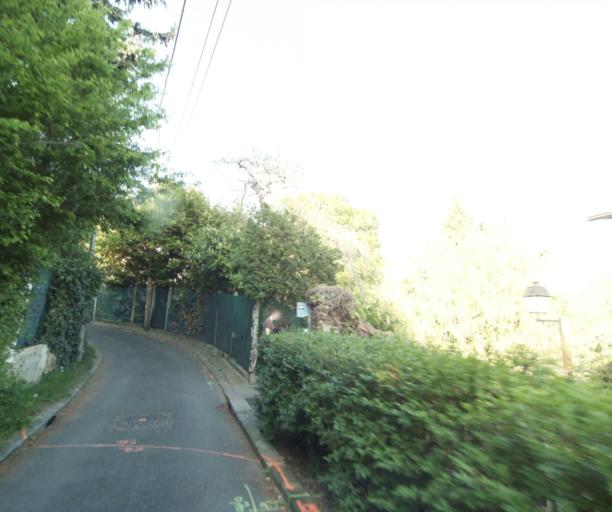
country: FR
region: Ile-de-France
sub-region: Departement des Hauts-de-Seine
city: Ville-d'Avray
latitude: 48.8216
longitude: 2.2012
